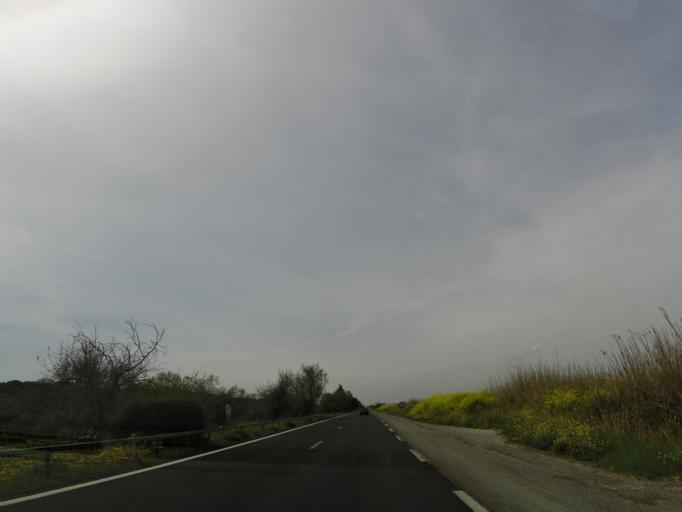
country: FR
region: Languedoc-Roussillon
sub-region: Departement de l'Herault
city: La Grande-Motte
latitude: 43.5656
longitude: 4.0549
